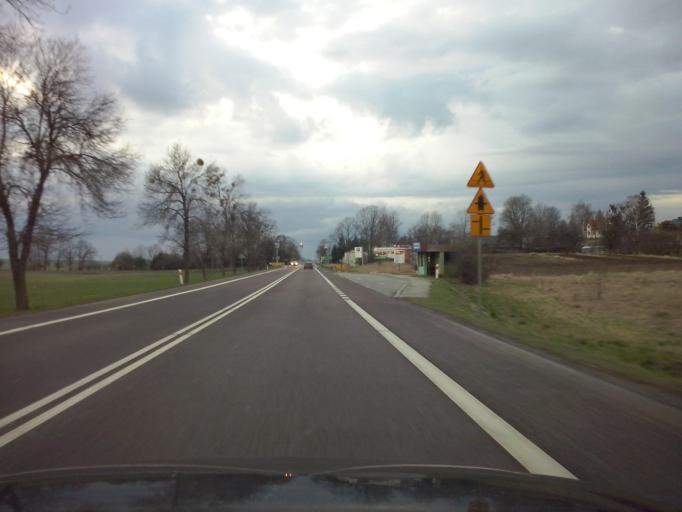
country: PL
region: Lublin Voivodeship
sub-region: Chelm
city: Chelm
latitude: 51.1623
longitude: 23.3892
